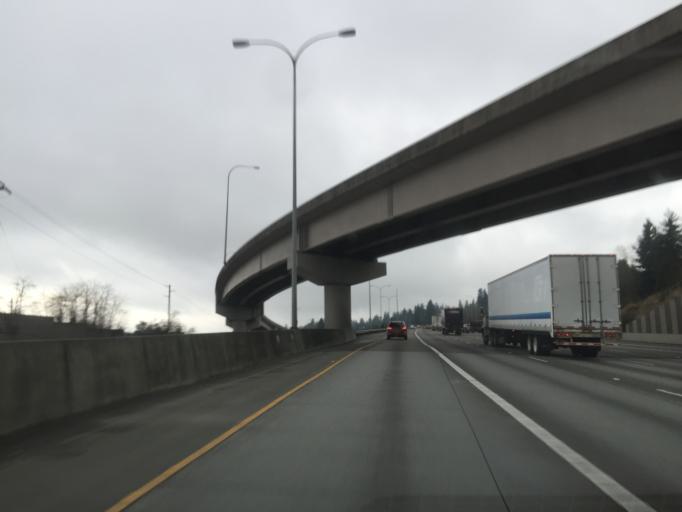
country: US
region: Washington
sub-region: Snohomish County
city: Everett
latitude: 47.9621
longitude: -122.1994
